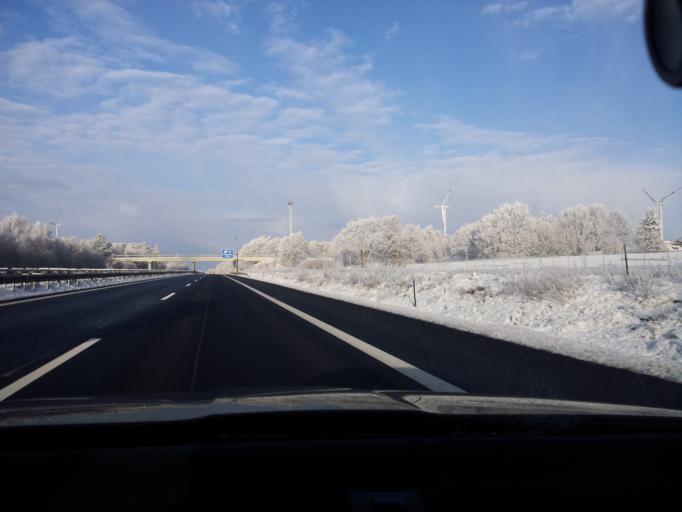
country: DE
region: Brandenburg
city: Gerdshagen
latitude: 53.2224
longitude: 12.2291
